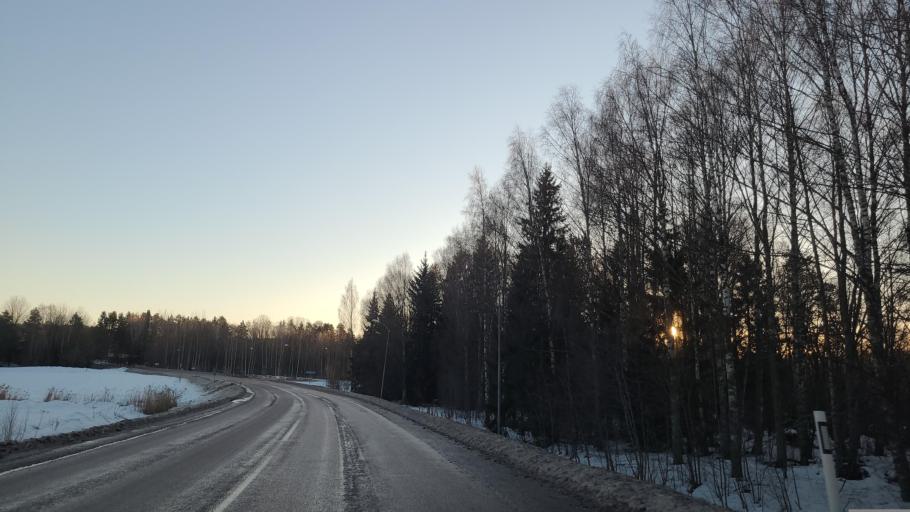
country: SE
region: Gaevleborg
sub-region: Soderhamns Kommun
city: Soderhamn
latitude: 61.2815
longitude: 16.9701
